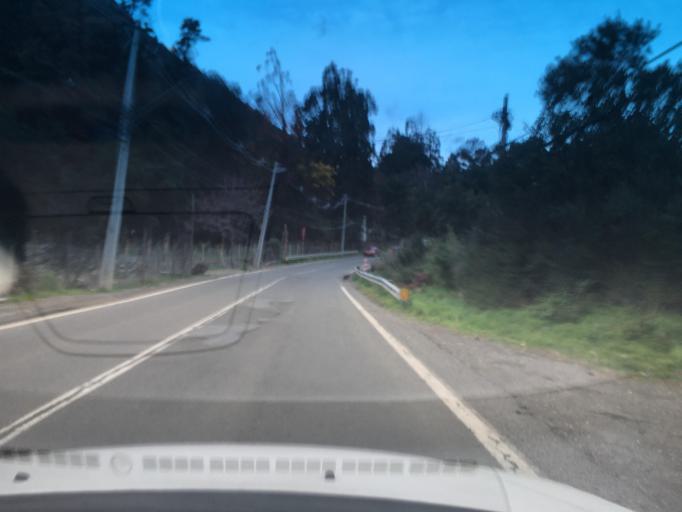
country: CL
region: Santiago Metropolitan
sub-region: Provincia de Cordillera
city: Puente Alto
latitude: -33.5773
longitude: -70.4376
